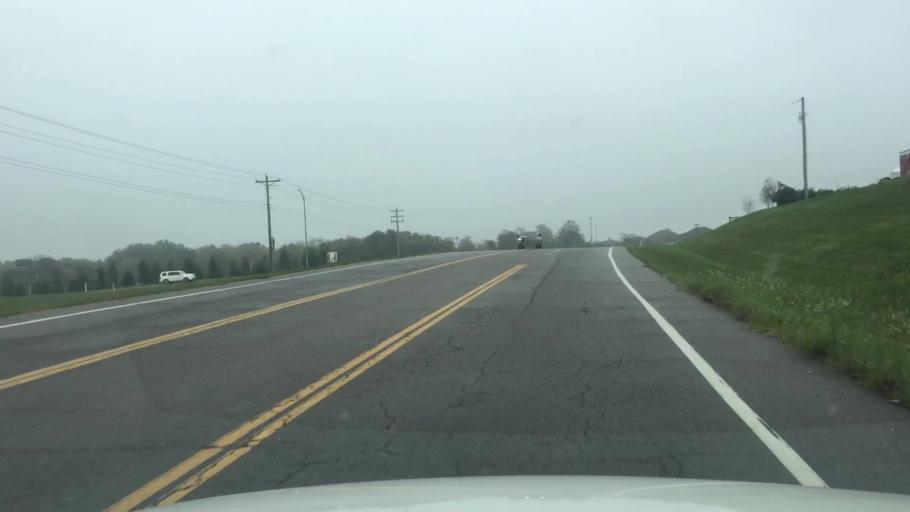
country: US
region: Missouri
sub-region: Boone County
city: Columbia
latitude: 38.8696
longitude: -92.4013
